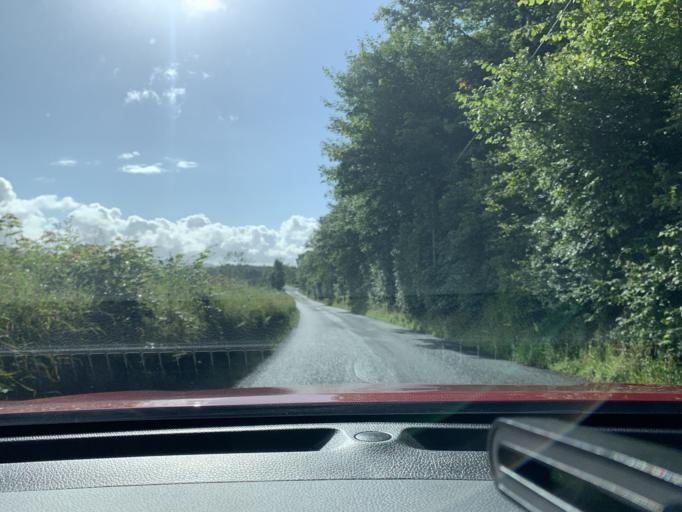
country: IE
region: Connaught
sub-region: Sligo
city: Strandhill
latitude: 54.3460
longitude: -8.5577
